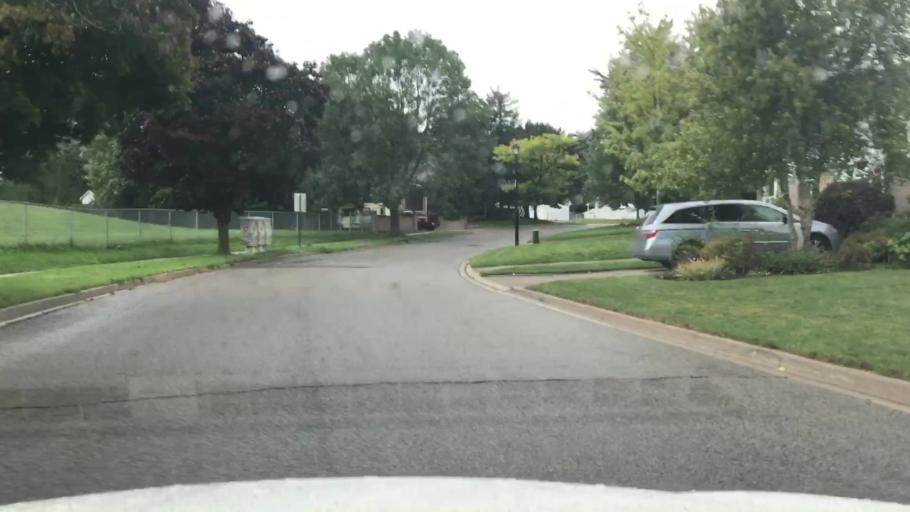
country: CA
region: Ontario
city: Newmarket
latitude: 44.0459
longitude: -79.4642
